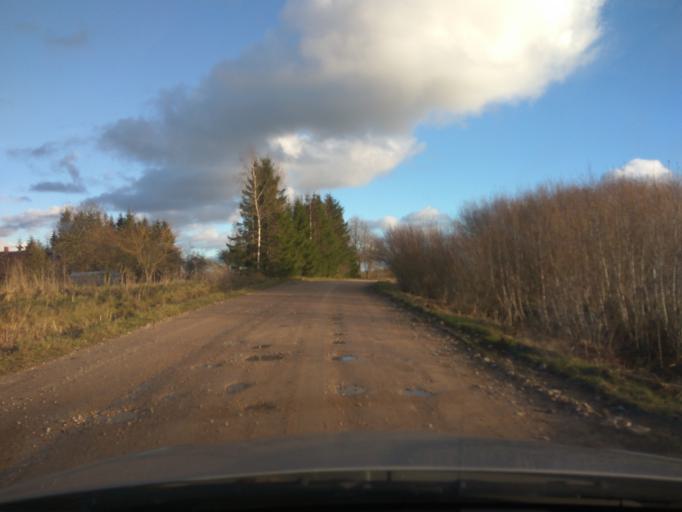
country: LV
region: Aizpute
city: Aizpute
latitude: 56.7486
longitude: 21.6069
